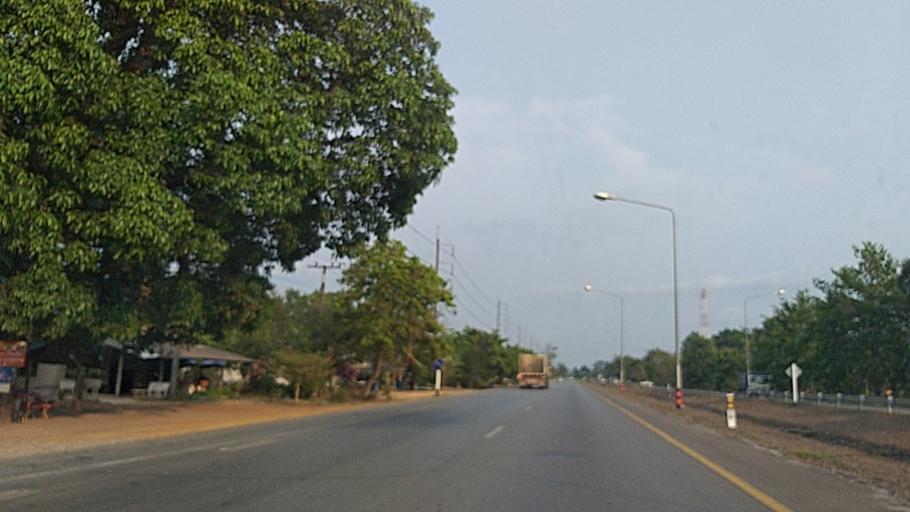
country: TH
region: Trat
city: Khao Saming
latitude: 12.4043
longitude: 102.3415
